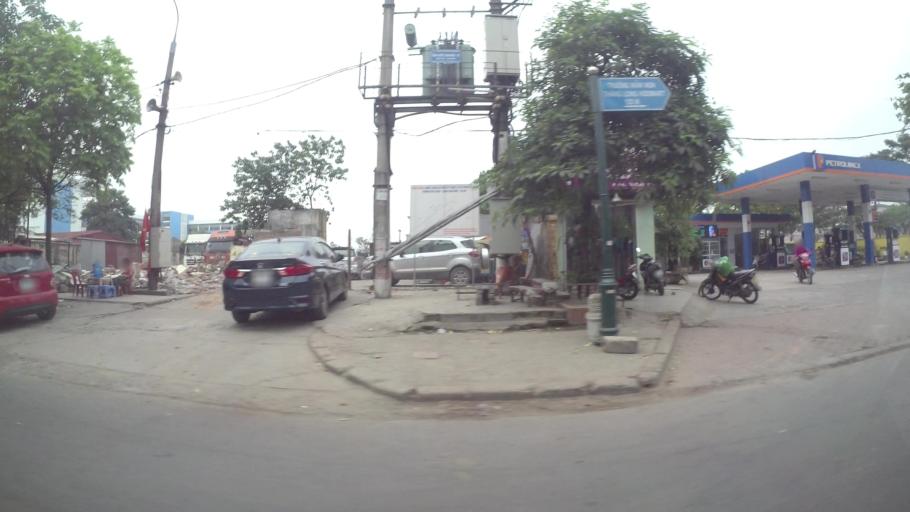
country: VN
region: Ha Noi
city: Hoan Kiem
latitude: 21.0682
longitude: 105.8900
